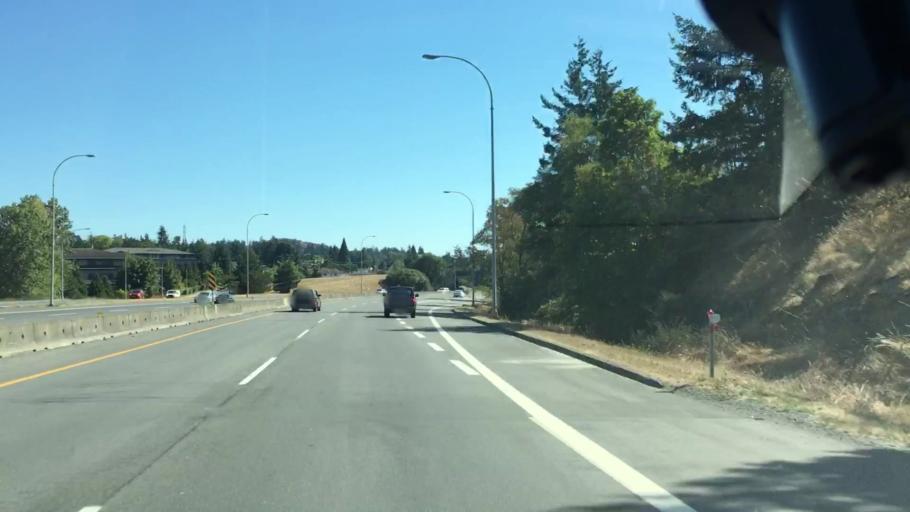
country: CA
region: British Columbia
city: Victoria
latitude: 48.4893
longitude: -123.3851
